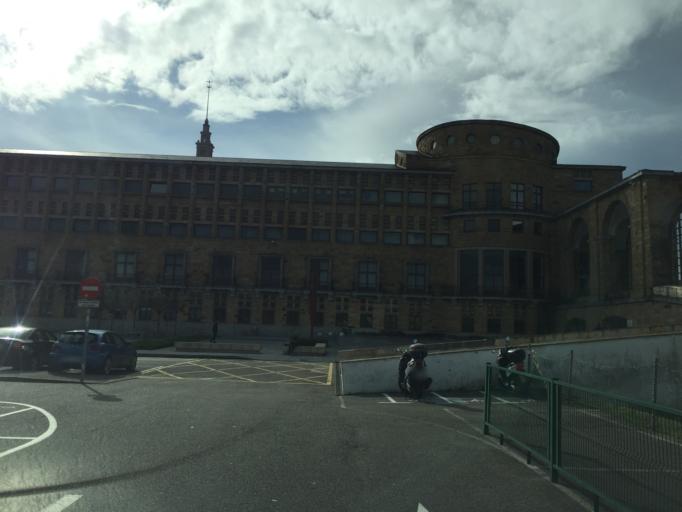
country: ES
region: Asturias
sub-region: Province of Asturias
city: Gijon
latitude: 43.5247
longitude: -5.6130
